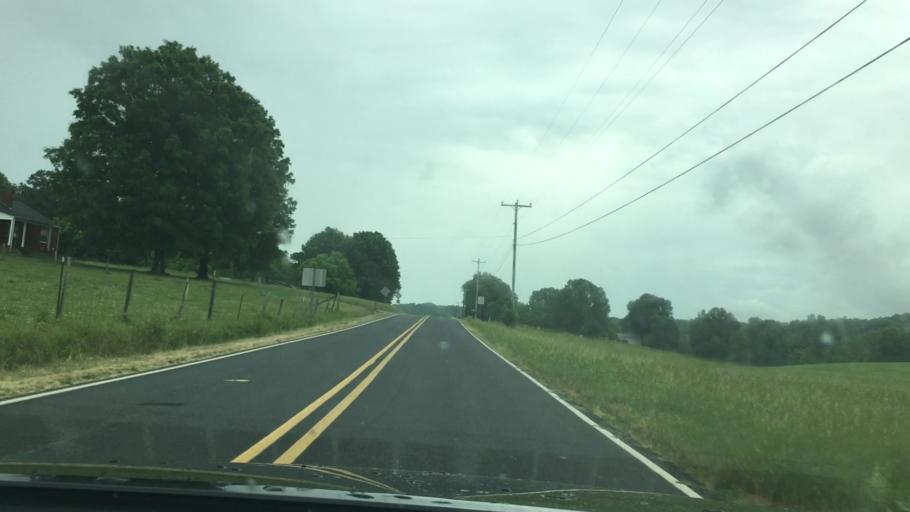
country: US
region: North Carolina
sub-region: Stanly County
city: Badin
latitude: 35.3728
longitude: -80.1170
